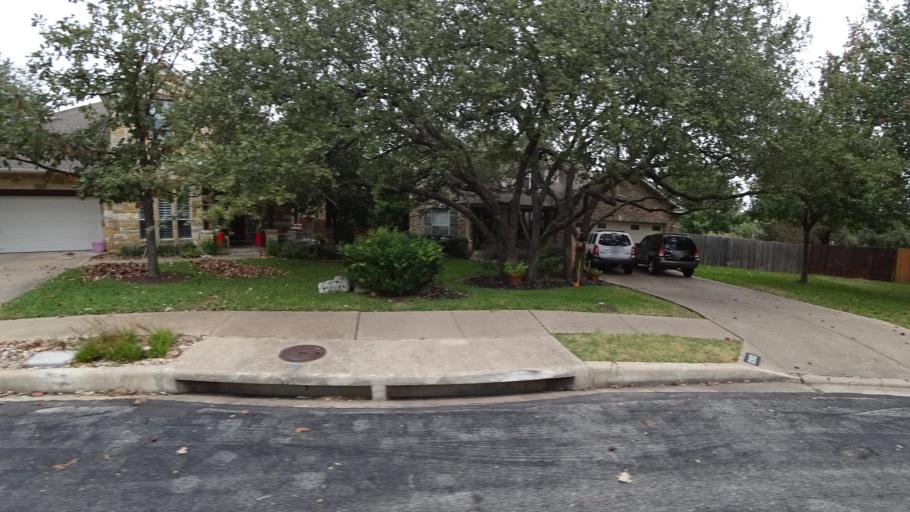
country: US
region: Texas
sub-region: Travis County
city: Shady Hollow
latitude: 30.1923
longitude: -97.8975
